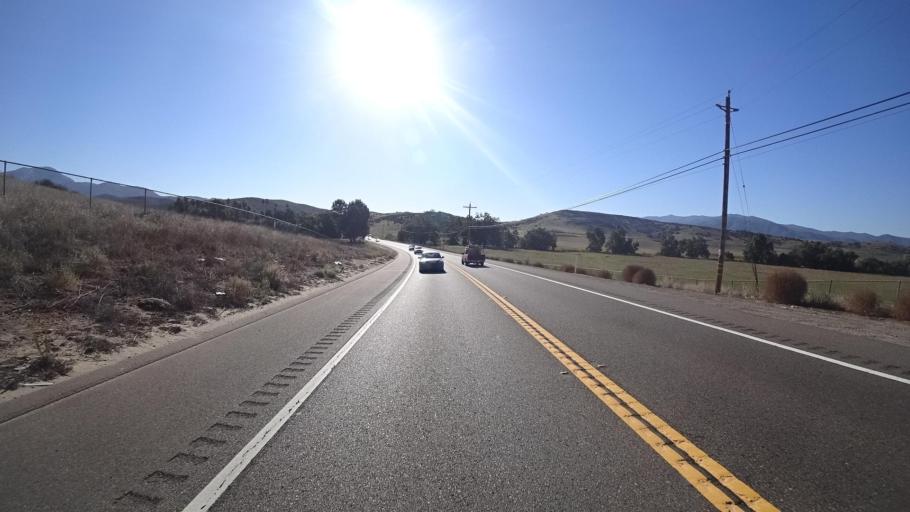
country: US
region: California
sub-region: San Diego County
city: Jamul
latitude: 32.6856
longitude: -116.8493
